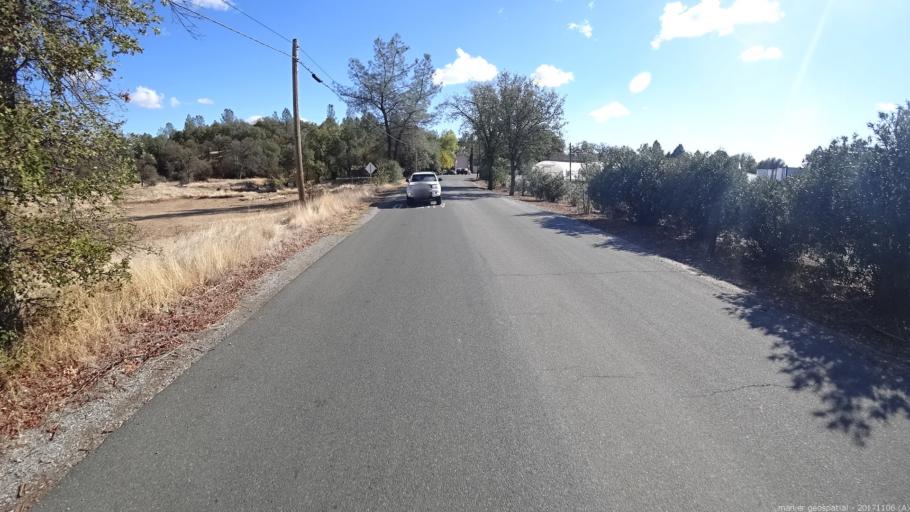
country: US
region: California
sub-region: Shasta County
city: Palo Cedro
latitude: 40.5881
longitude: -122.2977
